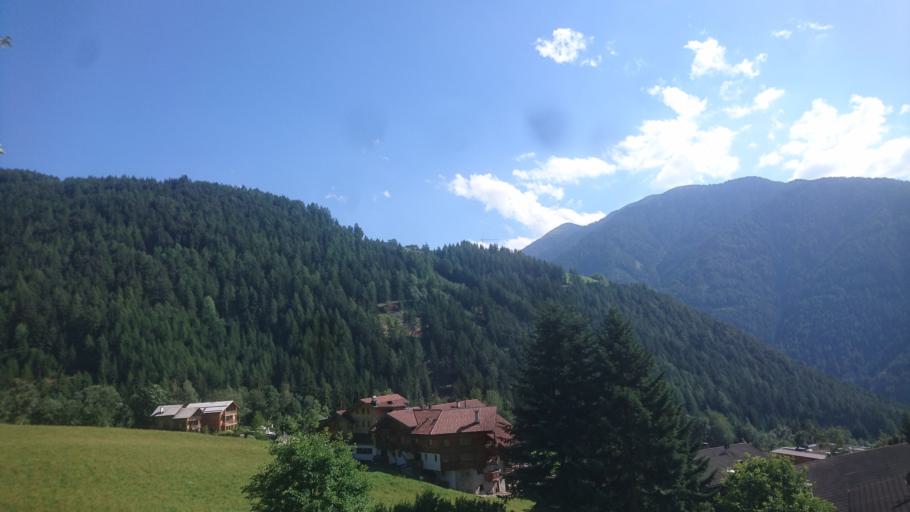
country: IT
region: Trentino-Alto Adige
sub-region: Bolzano
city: Villa
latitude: 46.7473
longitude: 11.7759
